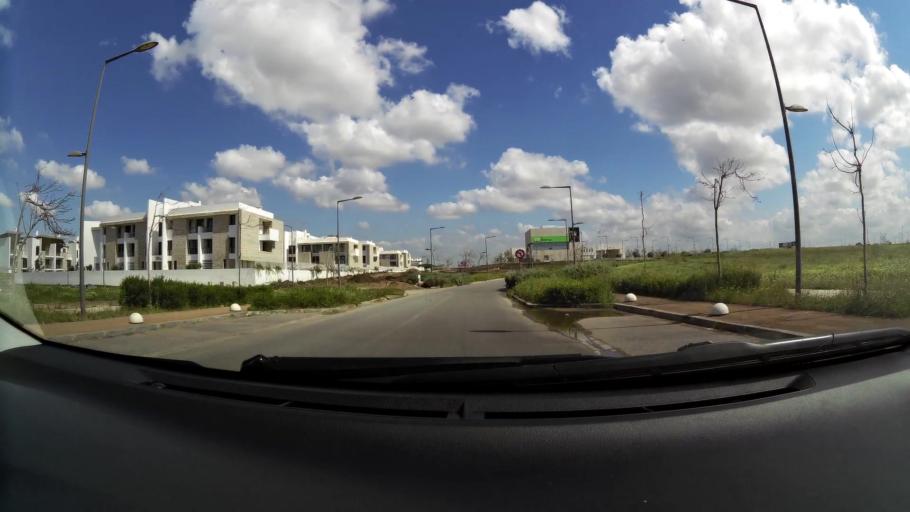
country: MA
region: Grand Casablanca
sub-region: Nouaceur
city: Bouskoura
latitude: 33.4953
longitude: -7.6040
